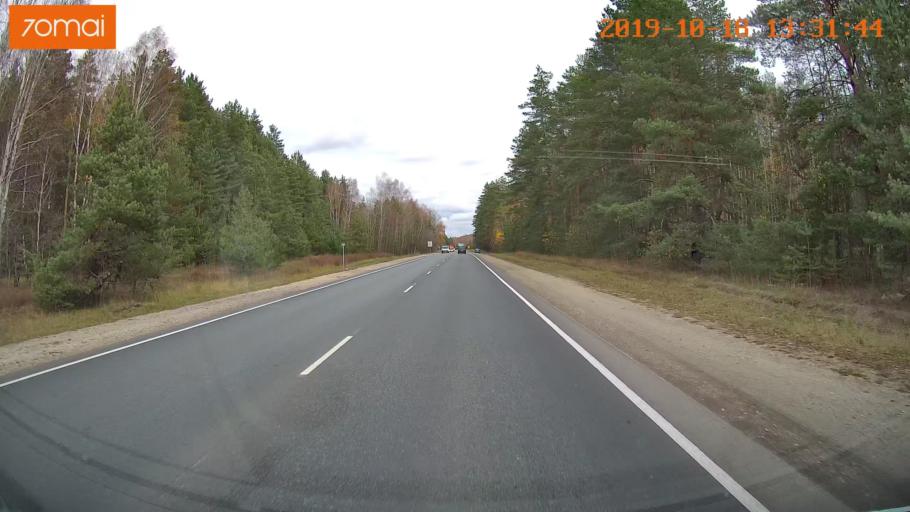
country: RU
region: Rjazan
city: Solotcha
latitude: 54.8251
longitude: 39.9061
